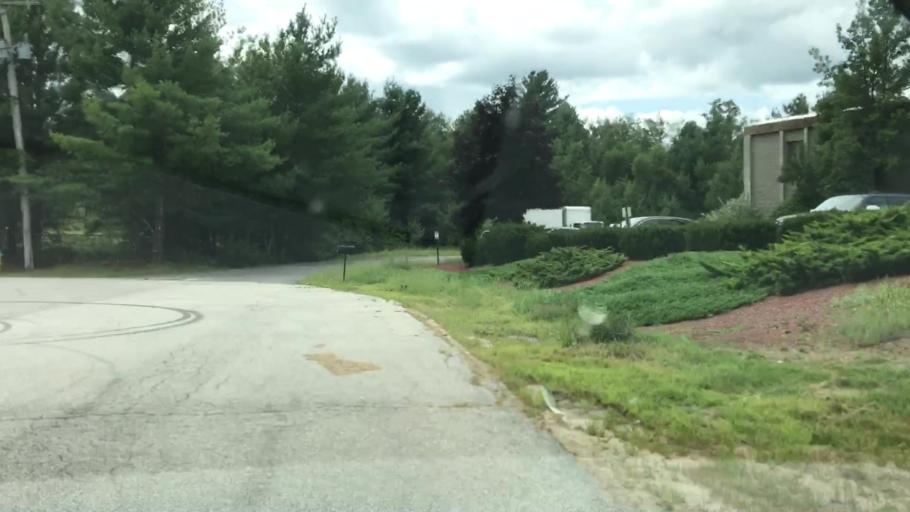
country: US
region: New Hampshire
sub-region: Hillsborough County
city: Hollis
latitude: 42.8018
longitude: -71.5860
